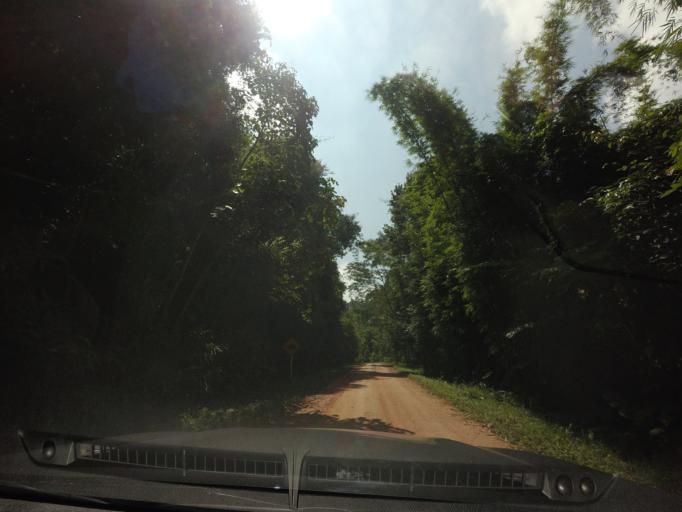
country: TH
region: Loei
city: Na Haeo
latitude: 17.5121
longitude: 100.9393
